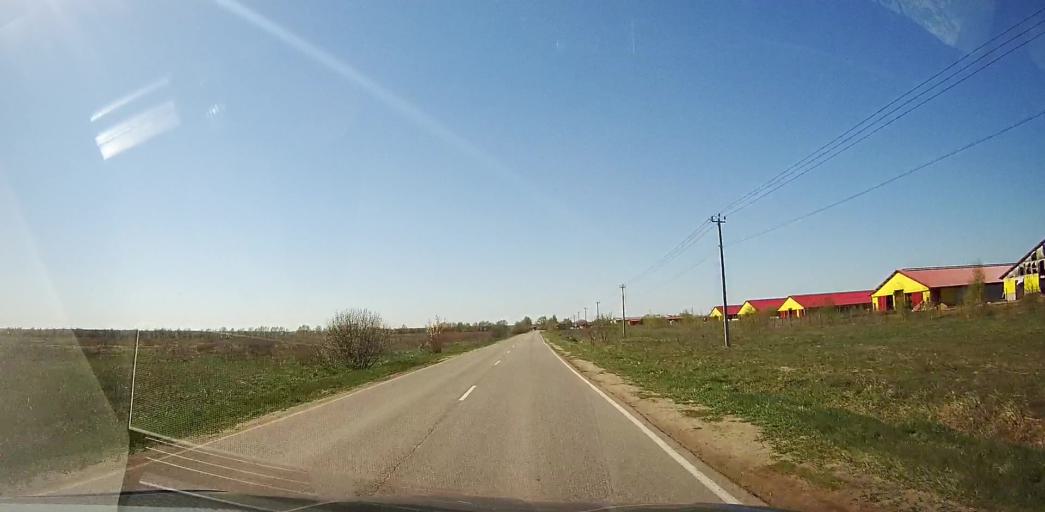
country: RU
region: Moskovskaya
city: Bronnitsy
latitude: 55.4761
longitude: 38.2490
